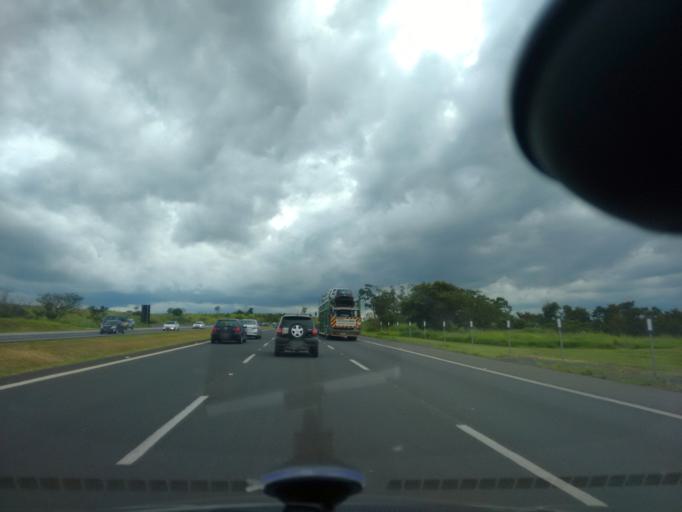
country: BR
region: Sao Paulo
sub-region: Campinas
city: Campinas
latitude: -22.9212
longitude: -47.1410
